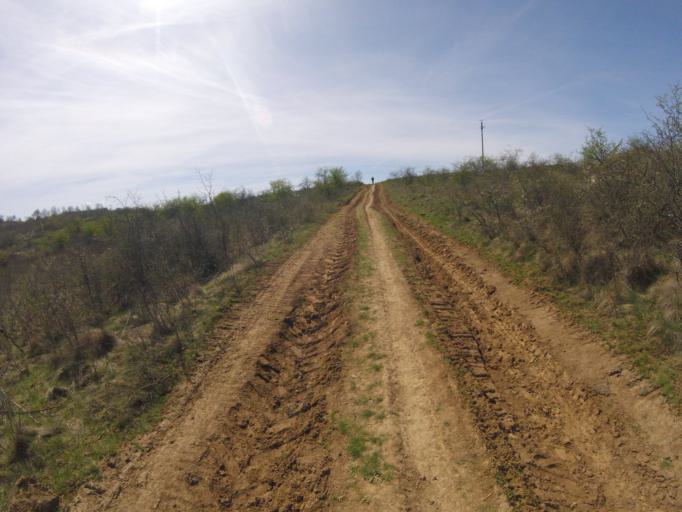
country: HU
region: Borsod-Abauj-Zemplen
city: Szendro
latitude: 48.4179
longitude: 20.7505
